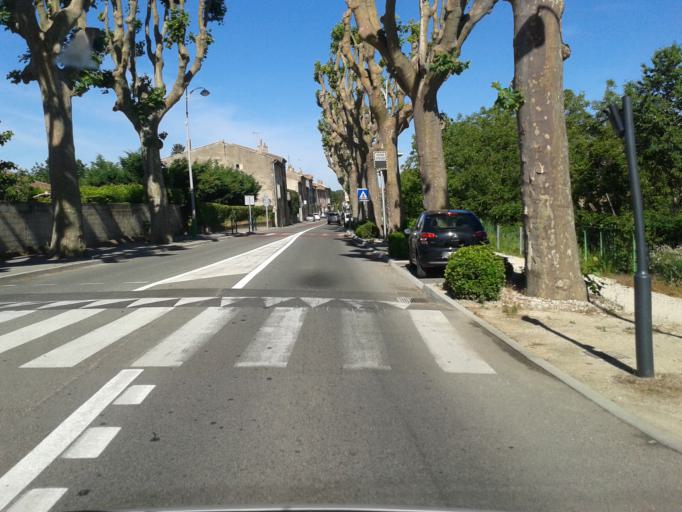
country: FR
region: Provence-Alpes-Cote d'Azur
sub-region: Departement des Bouches-du-Rhone
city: Peyrolles-en-Provence
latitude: 43.6463
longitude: 5.5891
